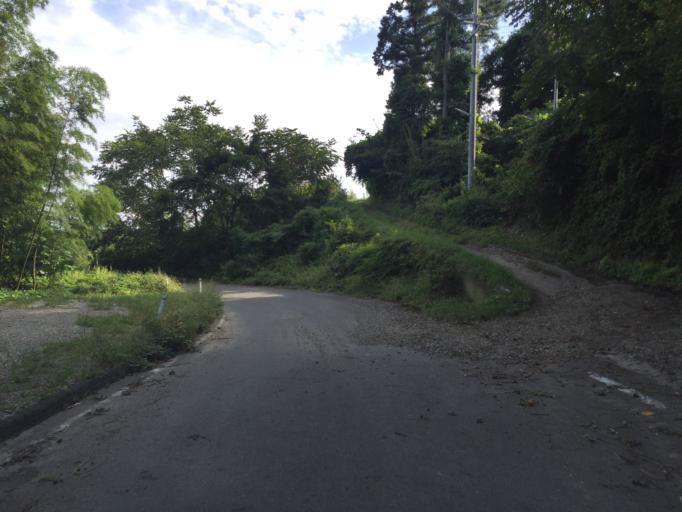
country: JP
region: Fukushima
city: Hobaramachi
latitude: 37.8356
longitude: 140.4690
